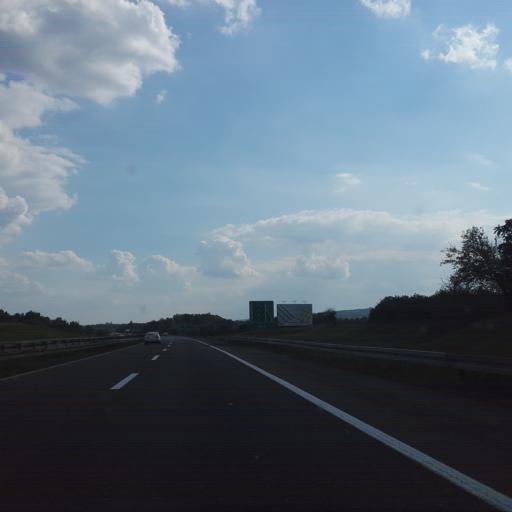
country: RS
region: Central Serbia
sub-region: Podunavski Okrug
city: Velika Plana
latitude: 44.3674
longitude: 21.0691
